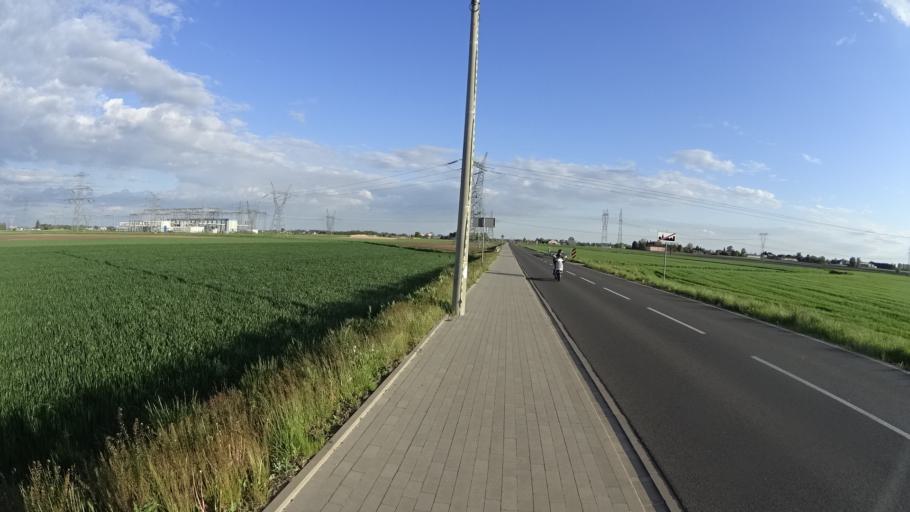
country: PL
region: Masovian Voivodeship
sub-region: Powiat warszawski zachodni
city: Jozefow
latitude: 52.2300
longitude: 20.7377
